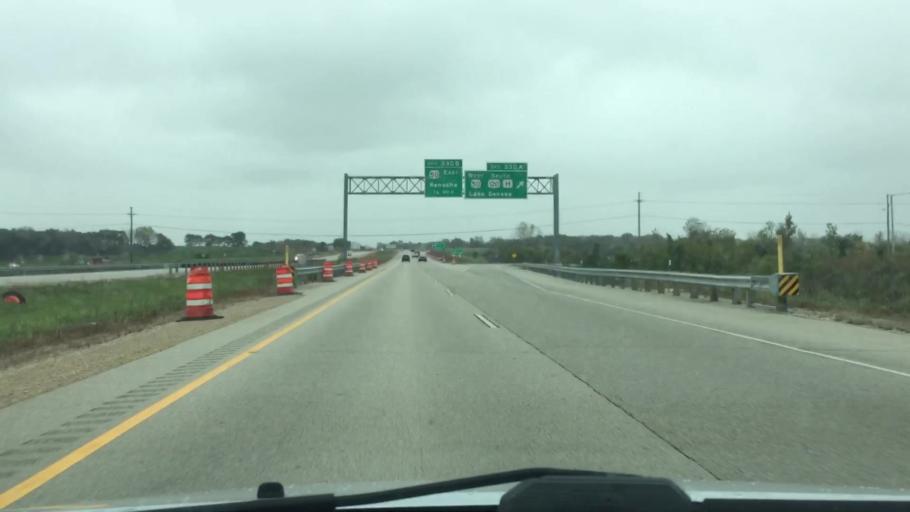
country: US
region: Wisconsin
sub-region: Walworth County
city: Lake Geneva
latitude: 42.5982
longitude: -88.4124
